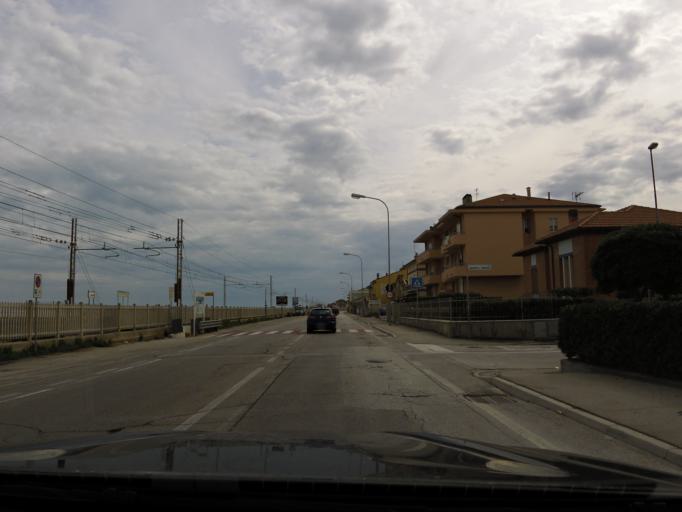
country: IT
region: The Marches
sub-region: Provincia di Macerata
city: Porto Potenza Picena
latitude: 43.3357
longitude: 13.7100
